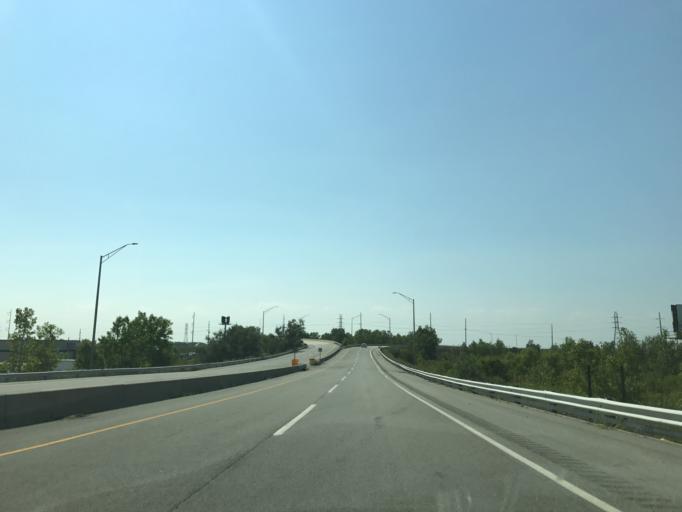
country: US
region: Indiana
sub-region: Lake County
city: Whiting
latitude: 41.6571
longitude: -87.5097
